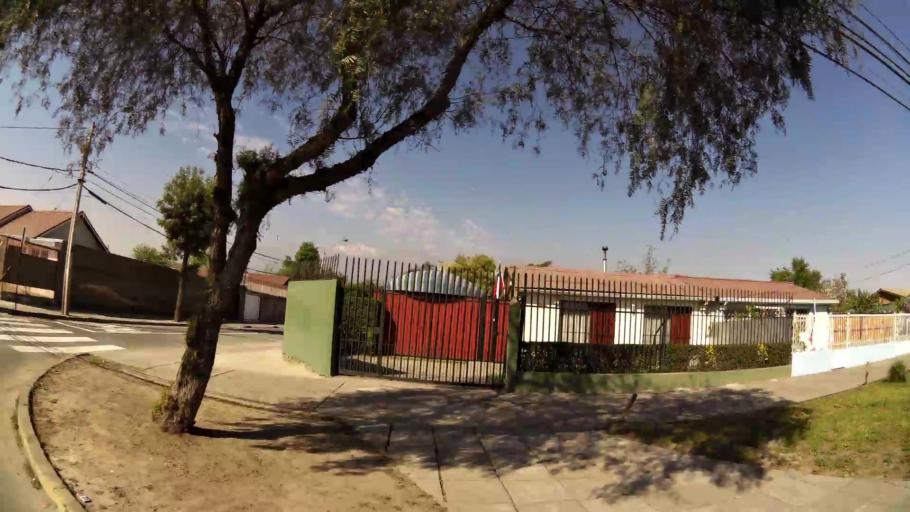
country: CL
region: Santiago Metropolitan
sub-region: Provincia de Santiago
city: La Pintana
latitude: -33.5243
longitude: -70.6098
